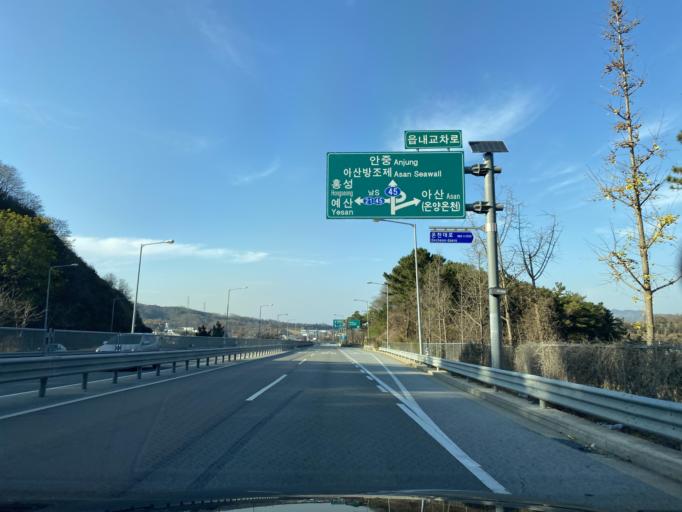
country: KR
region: Chungcheongnam-do
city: Asan
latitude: 36.7768
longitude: 126.9414
